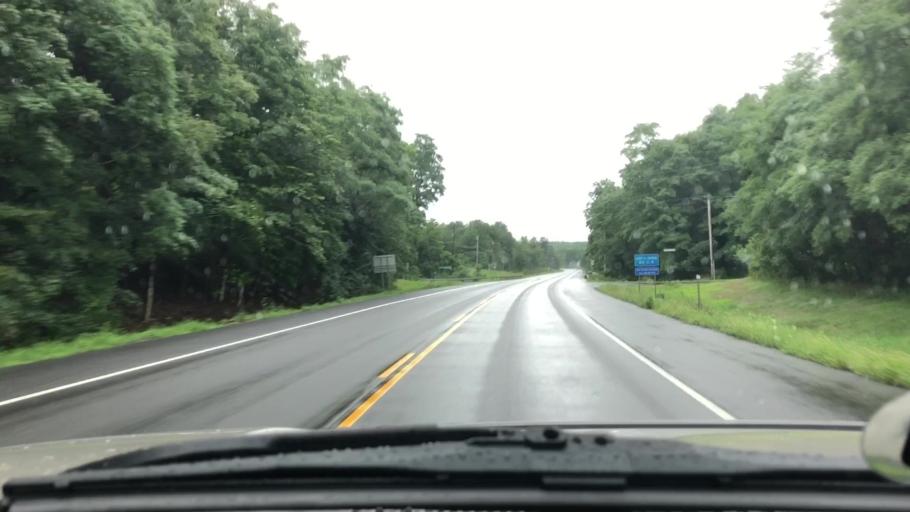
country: US
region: New York
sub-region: Greene County
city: Cairo
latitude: 42.3151
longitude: -74.0724
